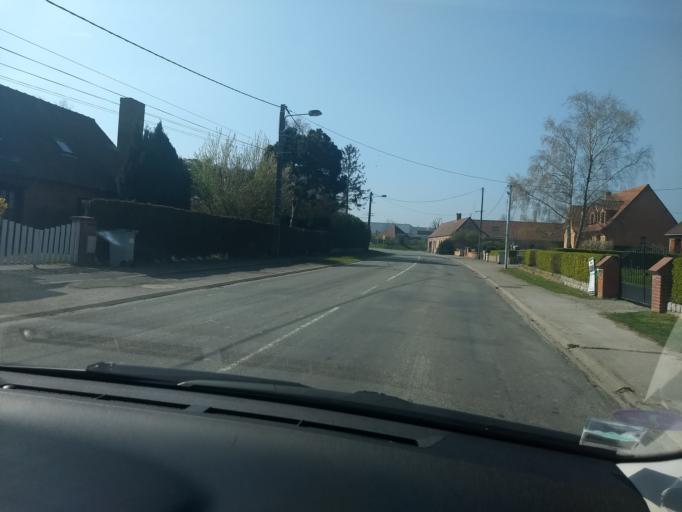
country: FR
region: Nord-Pas-de-Calais
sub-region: Departement du Pas-de-Calais
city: Tatinghem
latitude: 50.7413
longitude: 2.2034
